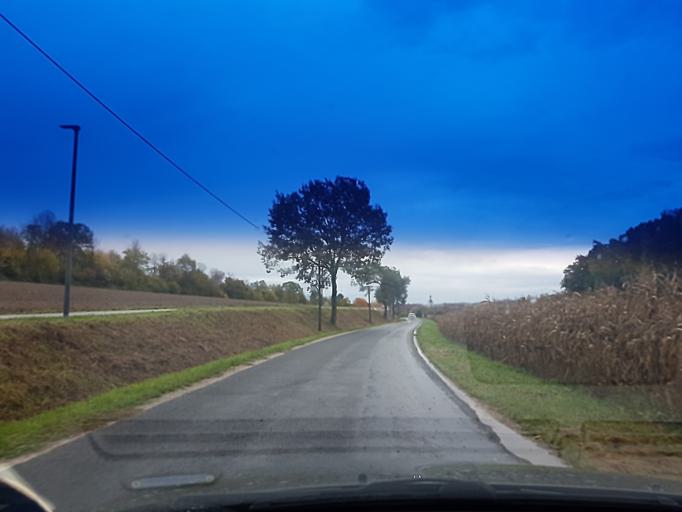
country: DE
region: Bavaria
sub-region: Regierungsbezirk Mittelfranken
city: Wachenroth
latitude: 49.7539
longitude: 10.7035
